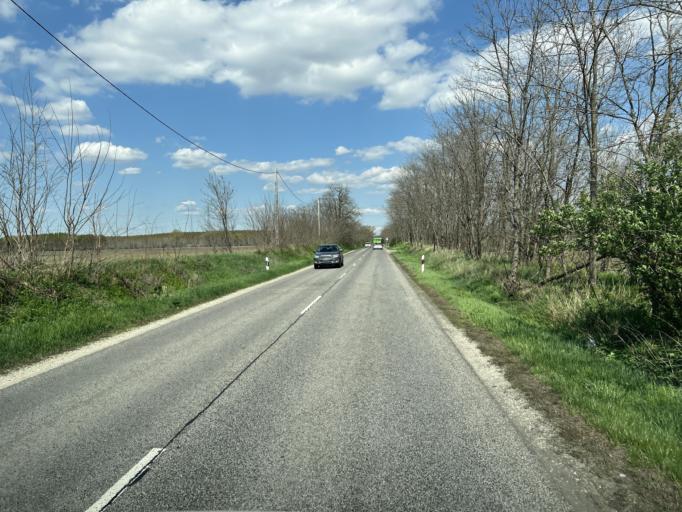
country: HU
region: Pest
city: Ullo
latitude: 47.3599
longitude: 19.3127
